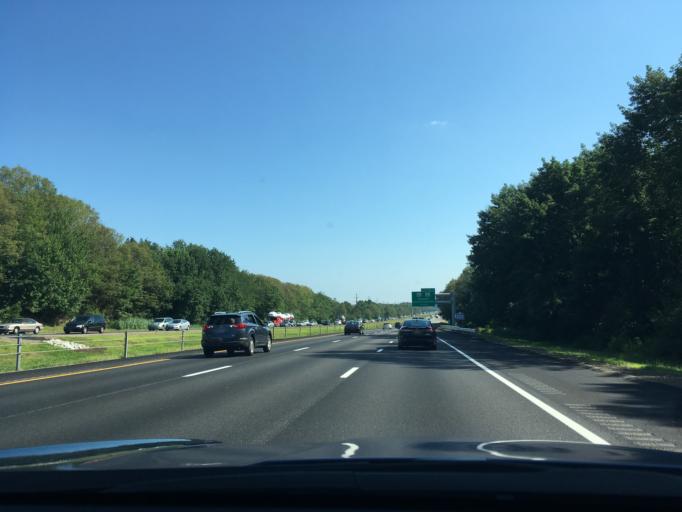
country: US
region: Rhode Island
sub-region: Kent County
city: East Greenwich
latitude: 41.6446
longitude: -71.4879
